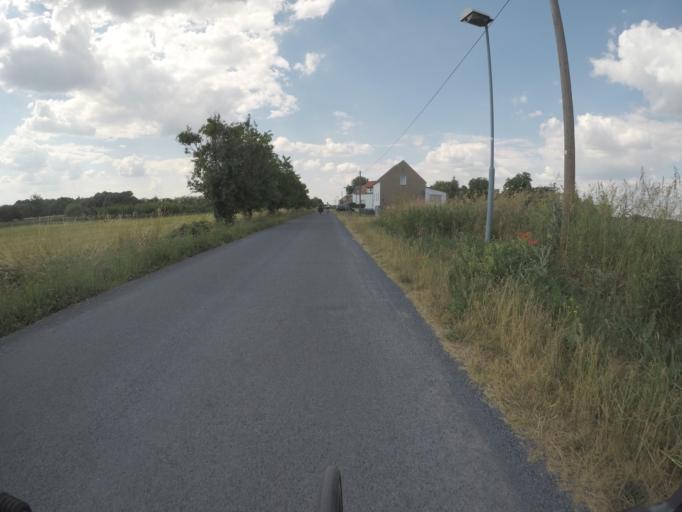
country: DE
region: Brandenburg
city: Roskow
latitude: 52.4501
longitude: 12.7670
